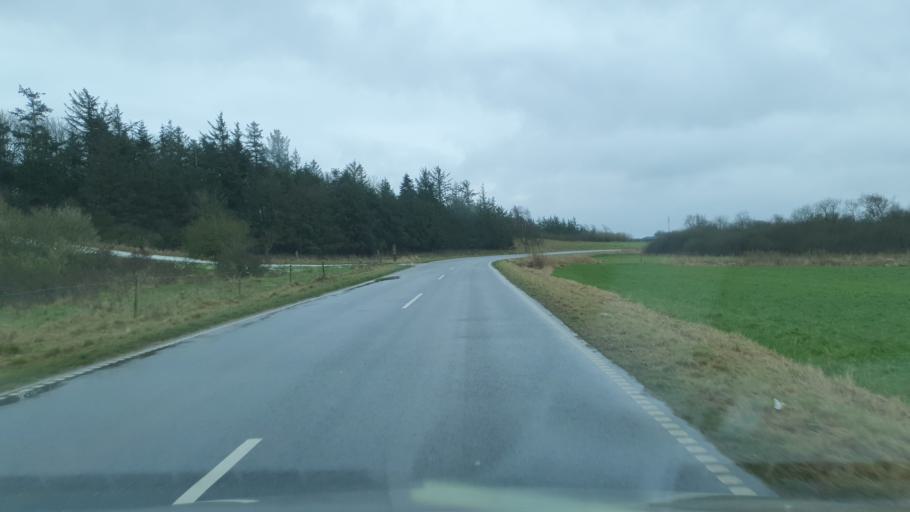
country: DK
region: North Denmark
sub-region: Jammerbugt Kommune
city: Fjerritslev
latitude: 57.1154
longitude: 9.1279
